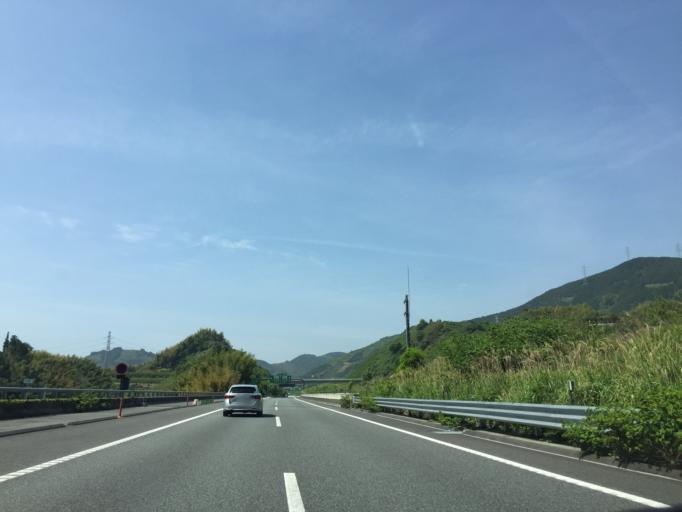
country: JP
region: Shizuoka
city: Shizuoka-shi
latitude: 35.0901
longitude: 138.4736
